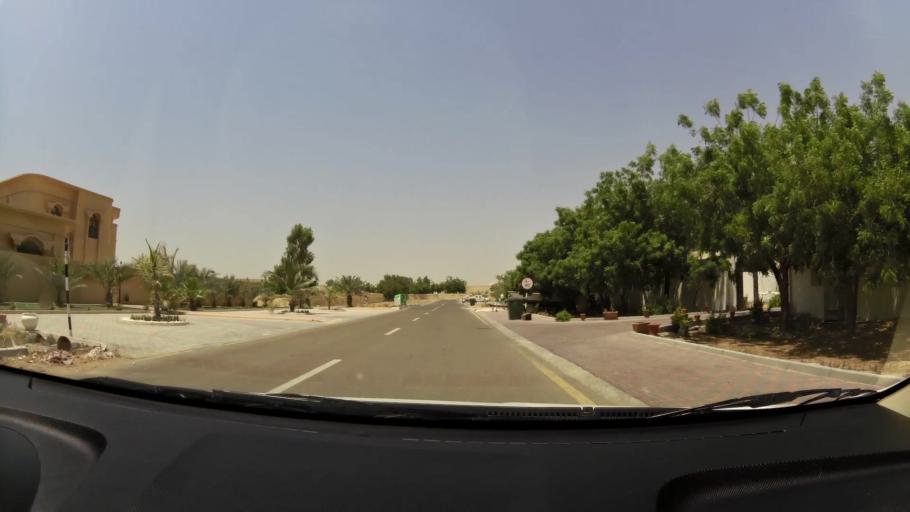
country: AE
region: Ajman
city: Ajman
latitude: 25.4208
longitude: 55.5041
